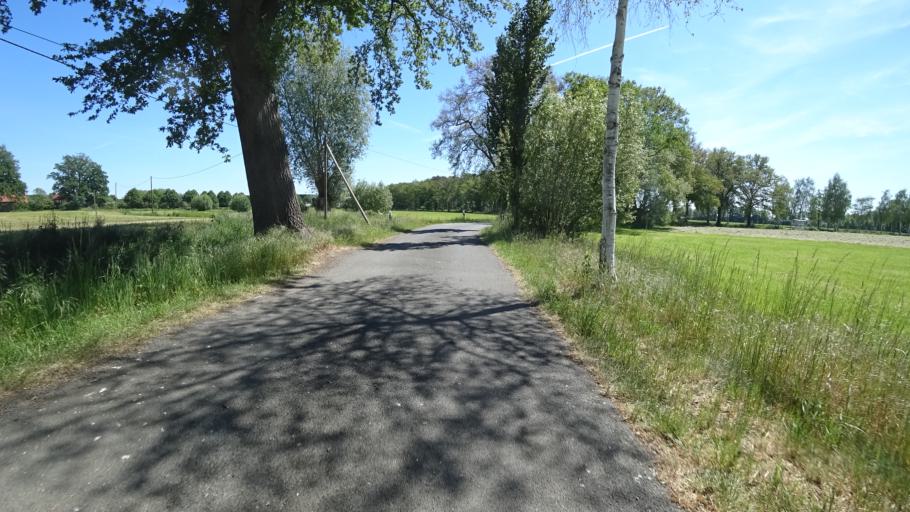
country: DE
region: North Rhine-Westphalia
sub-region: Regierungsbezirk Detmold
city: Guetersloh
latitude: 51.8588
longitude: 8.3622
